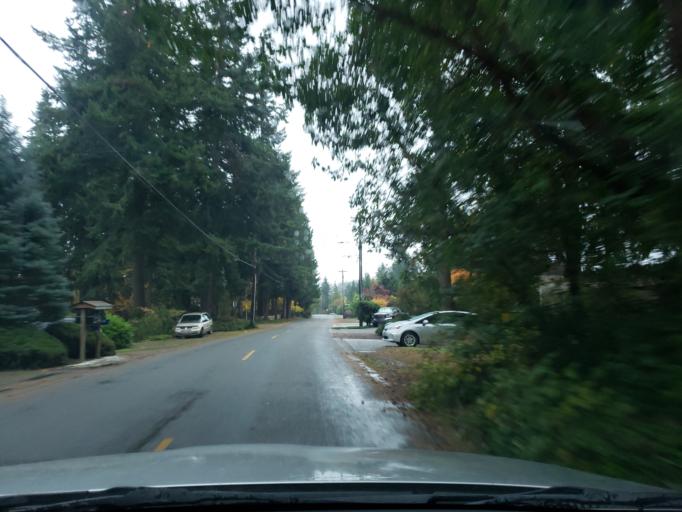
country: US
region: Washington
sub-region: Snohomish County
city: Meadowdale
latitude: 47.8376
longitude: -122.3303
